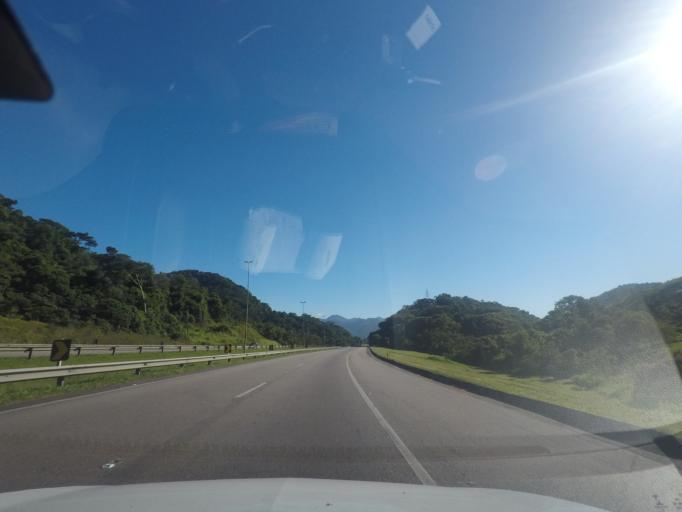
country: BR
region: Rio de Janeiro
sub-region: Guapimirim
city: Guapimirim
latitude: -22.5733
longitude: -43.0084
